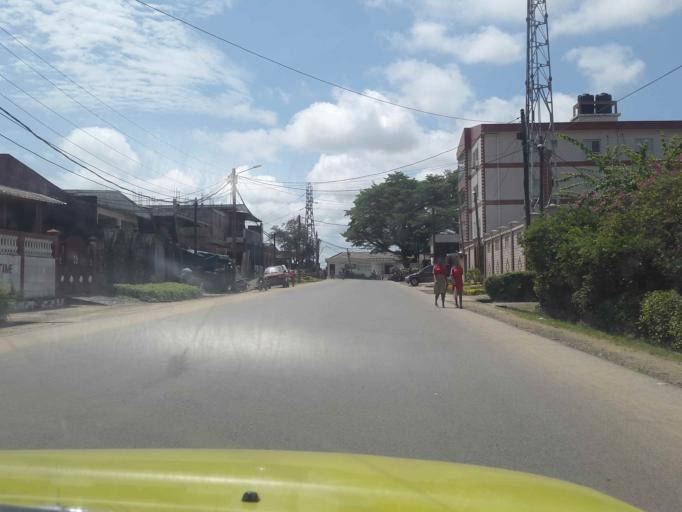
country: CM
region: Littoral
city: Douala
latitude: 4.0869
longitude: 9.7454
